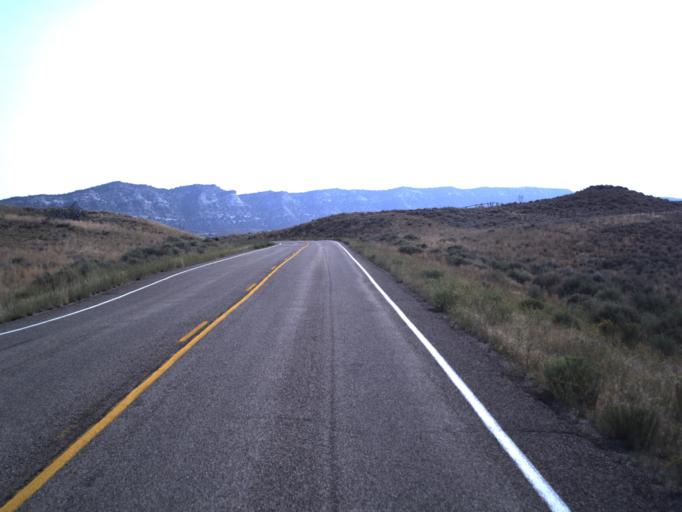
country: US
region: Utah
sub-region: Daggett County
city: Manila
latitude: 40.9851
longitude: -109.4404
